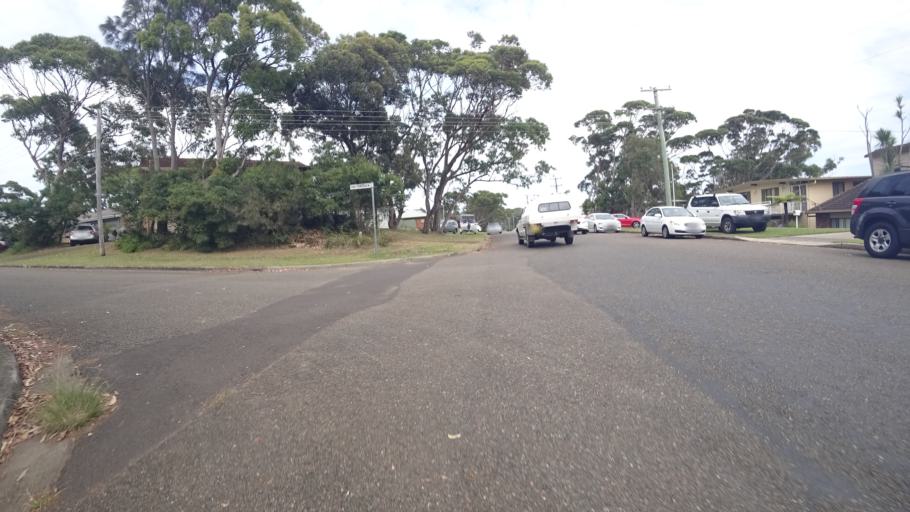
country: AU
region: New South Wales
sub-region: Shoalhaven Shire
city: Milton
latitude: -35.2558
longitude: 150.5202
